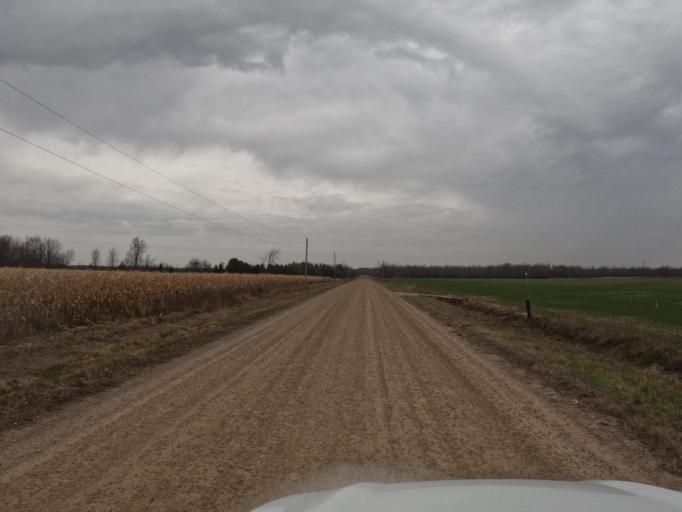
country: CA
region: Ontario
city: Shelburne
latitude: 43.8893
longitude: -80.3829
